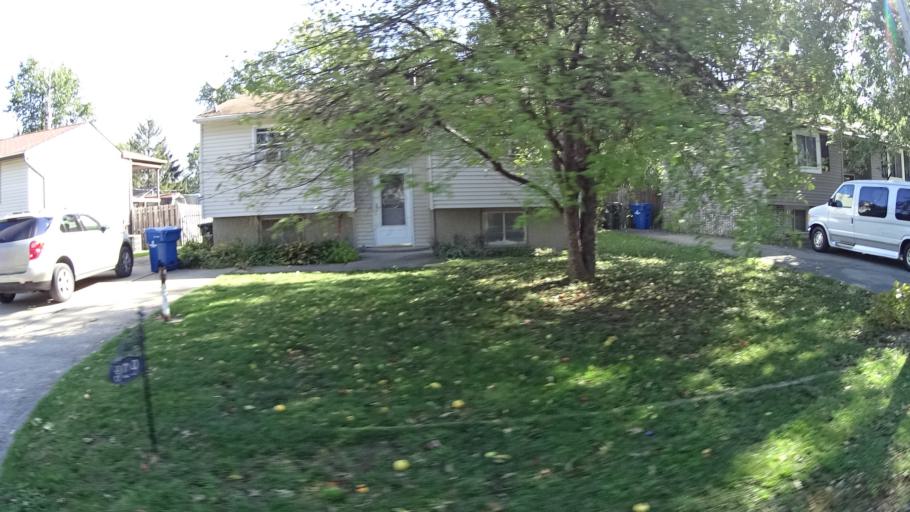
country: US
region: Ohio
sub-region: Lorain County
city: Vermilion-on-the-Lake
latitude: 41.4275
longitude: -82.3191
